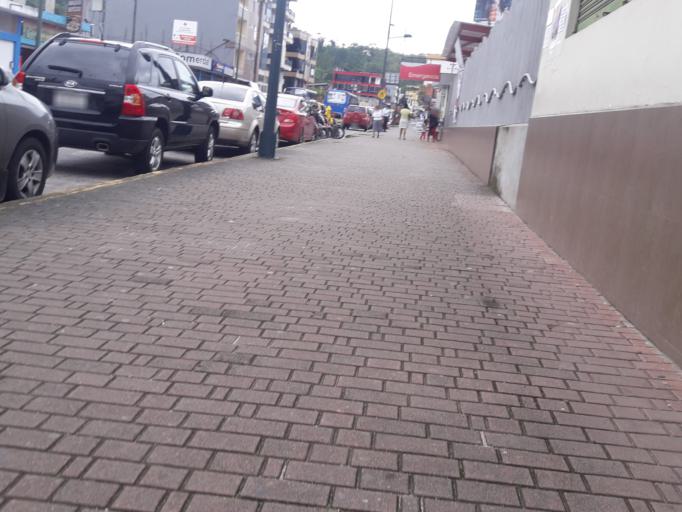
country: EC
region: Napo
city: Tena
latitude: -1.0039
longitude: -77.8110
